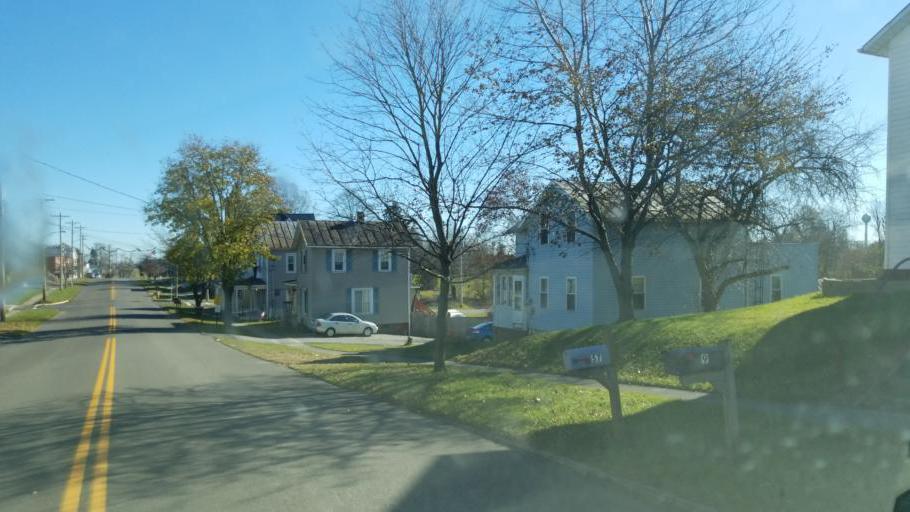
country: US
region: Ohio
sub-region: Huron County
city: Plymouth
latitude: 40.9680
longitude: -82.6044
